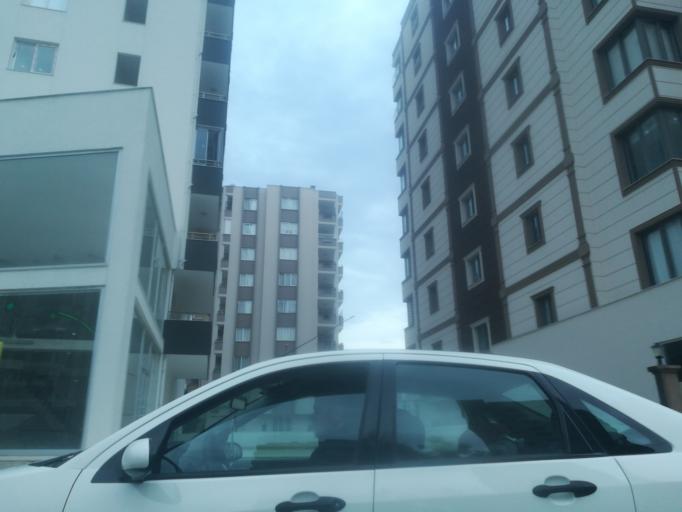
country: TR
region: Adana
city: Adana
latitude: 37.0442
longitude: 35.2911
